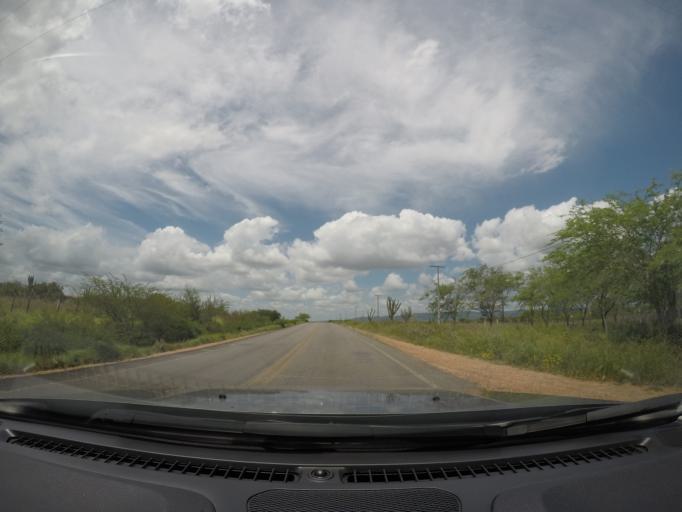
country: BR
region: Bahia
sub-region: Ipira
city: Ipira
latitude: -12.2287
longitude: -39.7890
